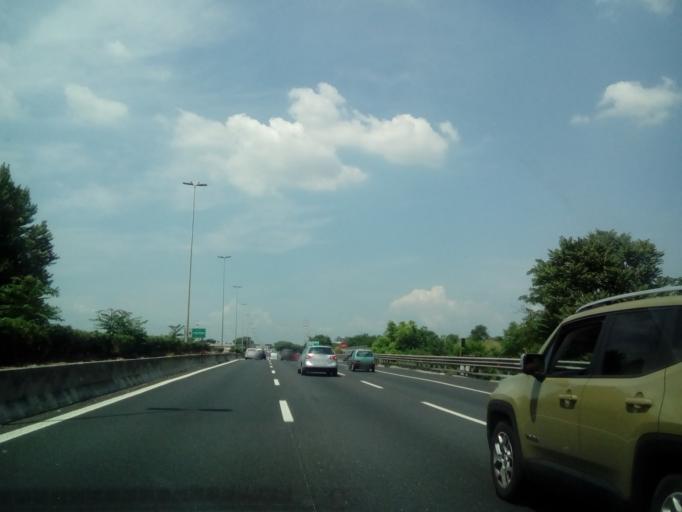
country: IT
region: Latium
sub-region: Citta metropolitana di Roma Capitale
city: Setteville
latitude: 41.8986
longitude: 12.6154
